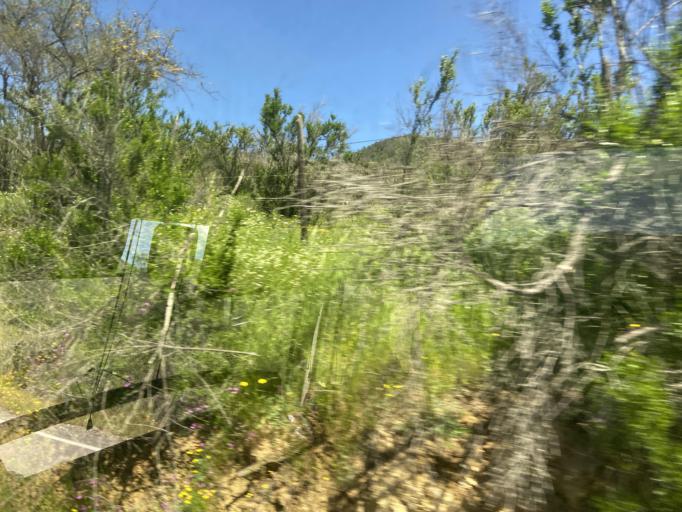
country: CL
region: Valparaiso
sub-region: Provincia de Marga Marga
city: Villa Alemana
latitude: -33.1799
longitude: -71.3063
